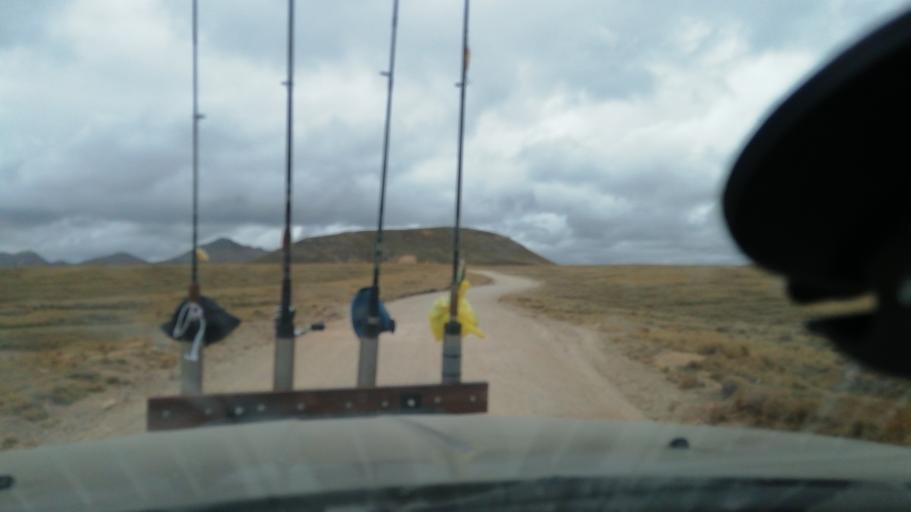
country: PE
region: Huancavelica
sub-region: Provincia de Huancavelica
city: Acobambilla
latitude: -12.5563
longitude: -75.5418
